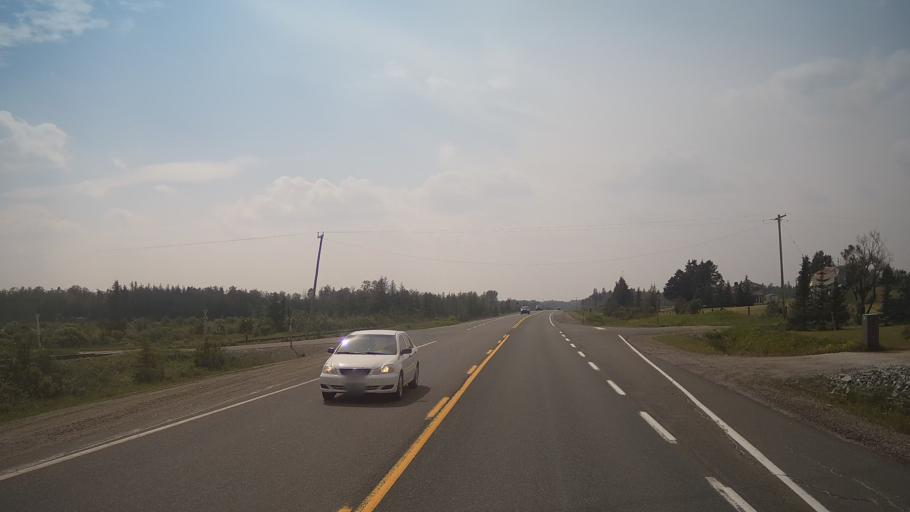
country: CA
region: Ontario
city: Kapuskasing
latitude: 49.3857
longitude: -82.3182
